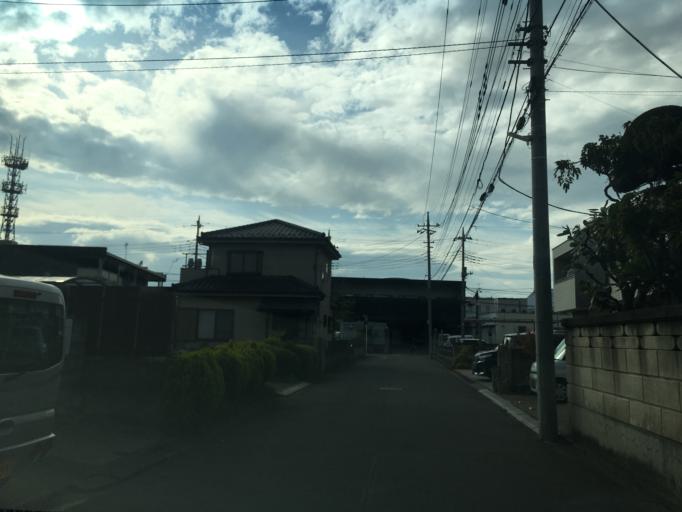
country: JP
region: Saitama
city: Tokorozawa
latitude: 35.7977
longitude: 139.4561
